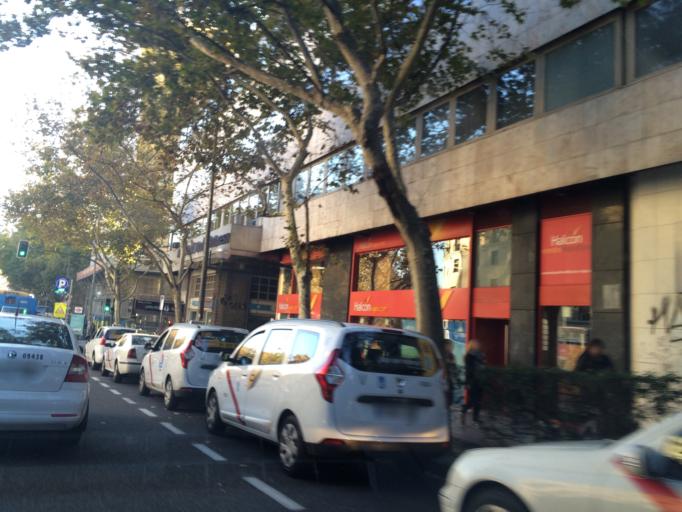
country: ES
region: Madrid
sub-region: Provincia de Madrid
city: Chamberi
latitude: 40.4276
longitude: -3.7142
